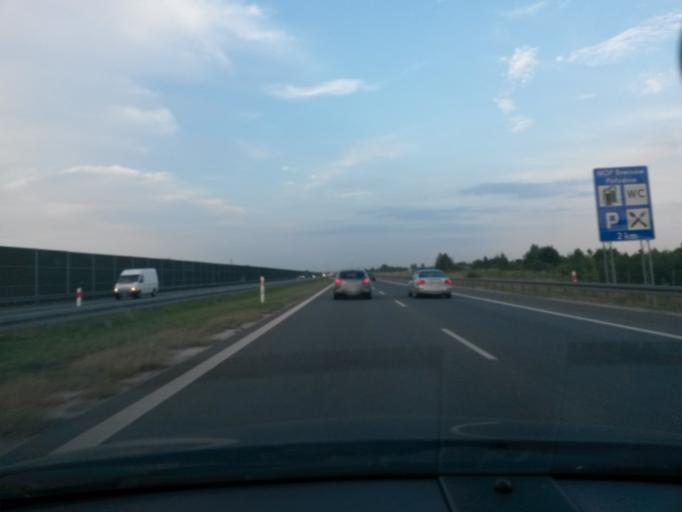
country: PL
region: Masovian Voivodeship
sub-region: Powiat grodziski
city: Milanowek
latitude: 52.1496
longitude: 20.6494
